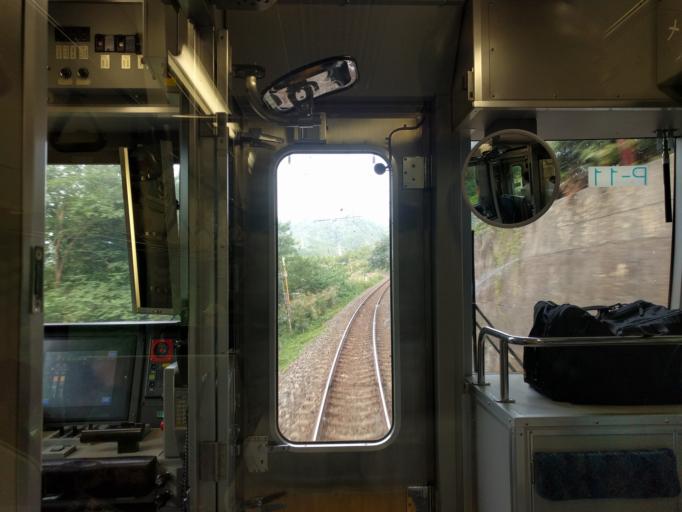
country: JP
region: Fukushima
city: Inawashiro
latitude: 37.4947
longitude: 140.2251
